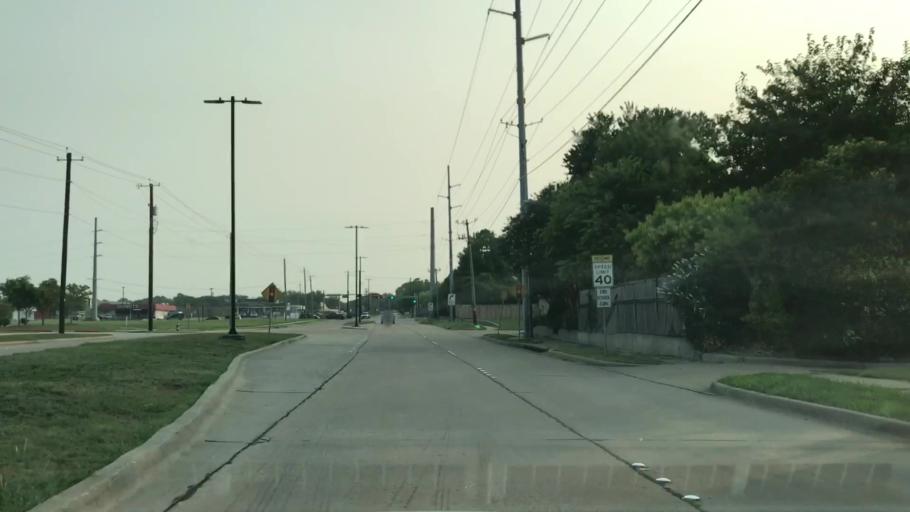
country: US
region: Texas
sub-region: Dallas County
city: Garland
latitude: 32.9313
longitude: -96.6127
